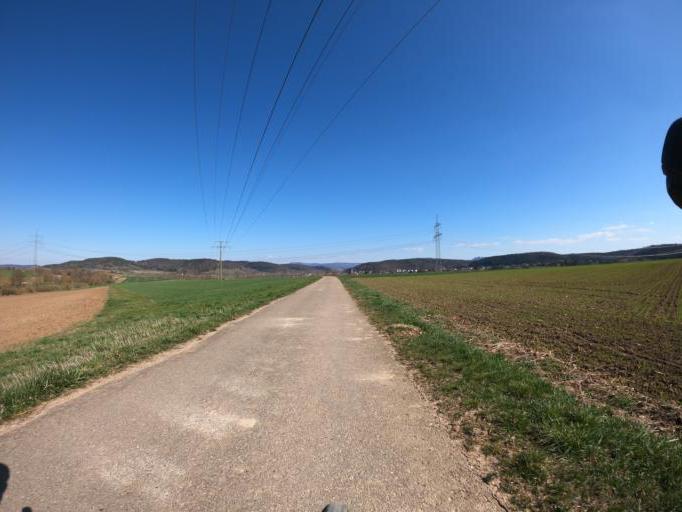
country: DE
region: Baden-Wuerttemberg
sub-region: Tuebingen Region
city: Rangendingen
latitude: 48.3848
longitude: 8.8625
